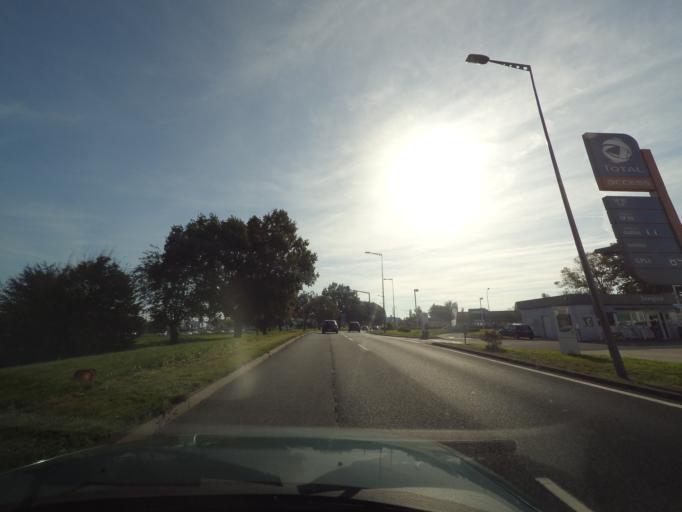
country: FR
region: Pays de la Loire
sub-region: Departement de Maine-et-Loire
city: Cholet
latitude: 47.0723
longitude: -0.8570
